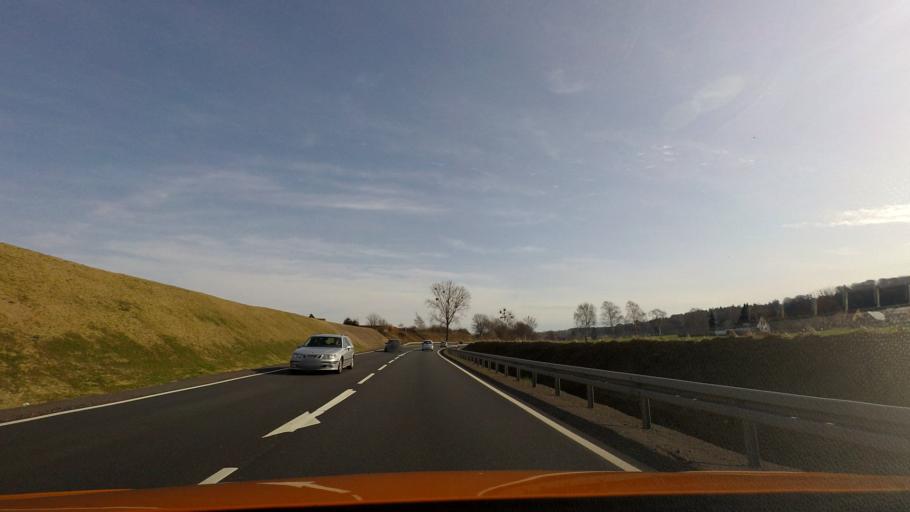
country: DE
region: Lower Saxony
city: Heuerssen
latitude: 52.3368
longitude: 9.2873
